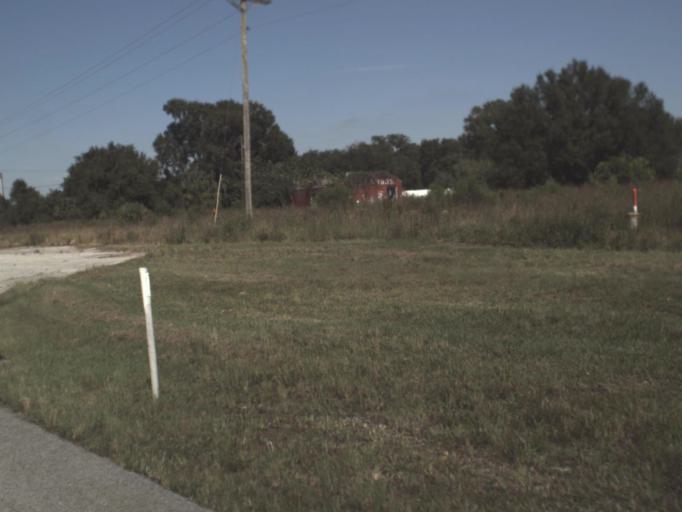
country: US
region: Florida
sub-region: Hendry County
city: Port LaBelle
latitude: 26.9388
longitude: -81.3164
